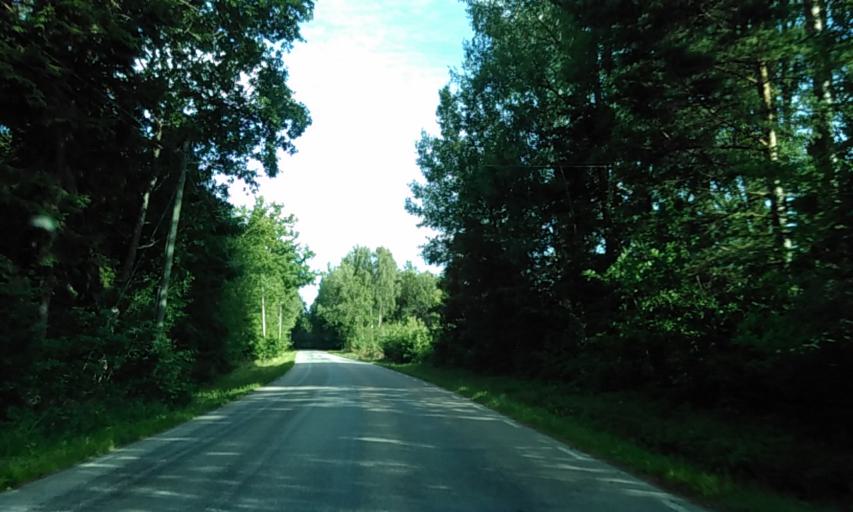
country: SE
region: Vaestra Goetaland
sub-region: Vara Kommun
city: Vara
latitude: 58.3562
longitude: 12.8699
